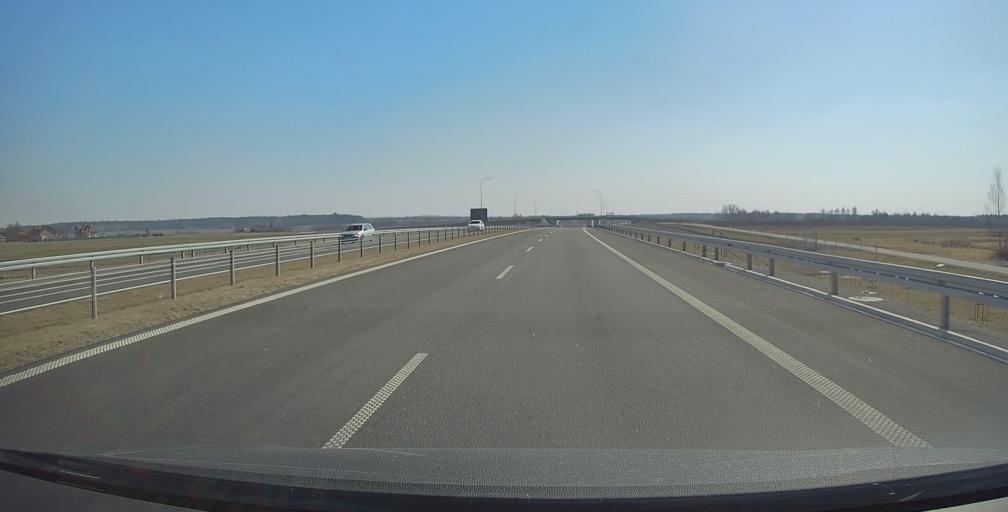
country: PL
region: Lublin Voivodeship
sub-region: Powiat janowski
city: Modliborzyce
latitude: 50.7353
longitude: 22.3428
